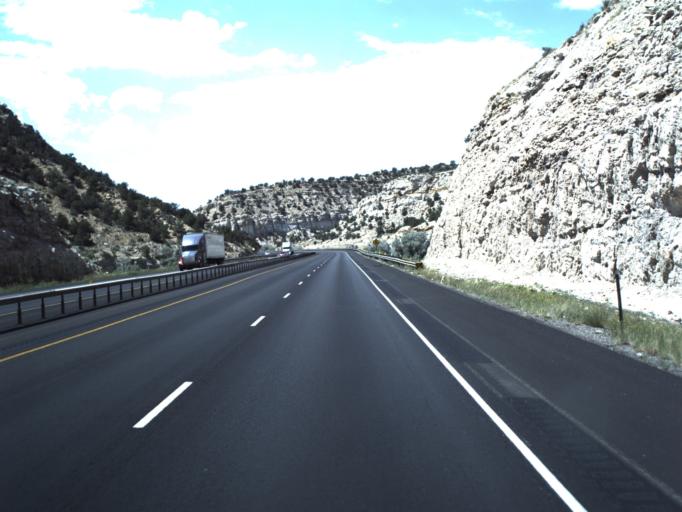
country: US
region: Utah
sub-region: Sevier County
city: Salina
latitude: 38.9084
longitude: -111.6987
